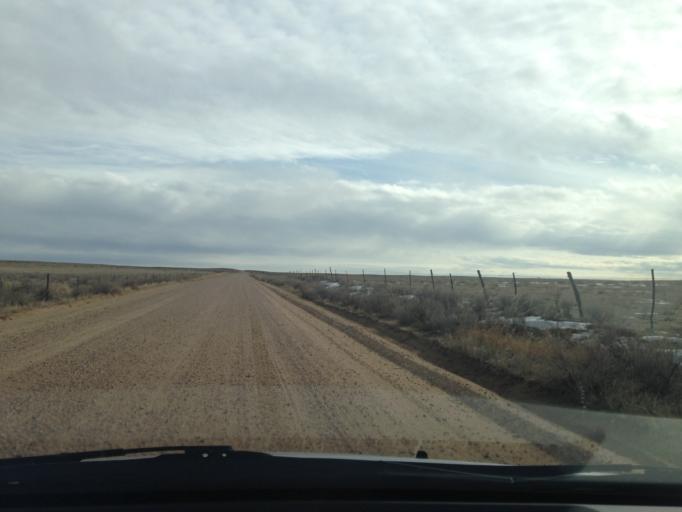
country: US
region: Colorado
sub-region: Weld County
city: Keenesburg
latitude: 40.2641
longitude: -104.2068
